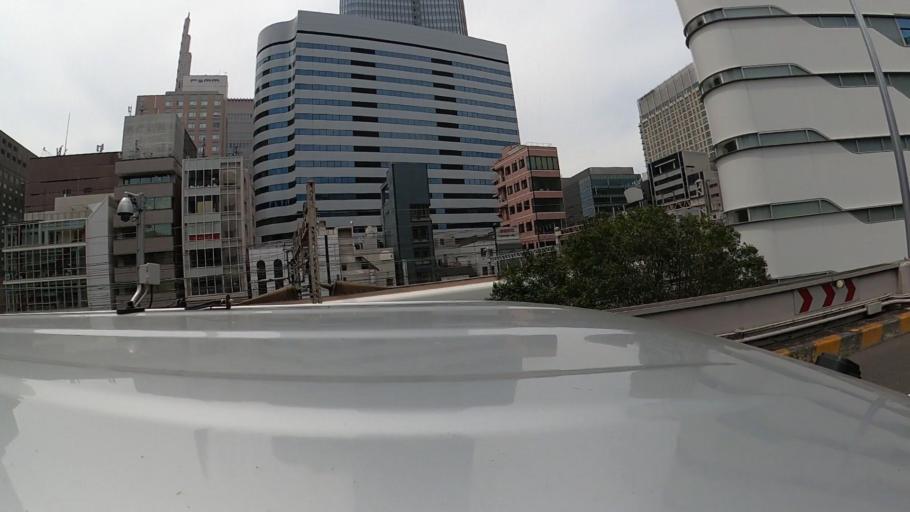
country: JP
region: Tokyo
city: Tokyo
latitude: 35.6724
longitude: 139.7607
